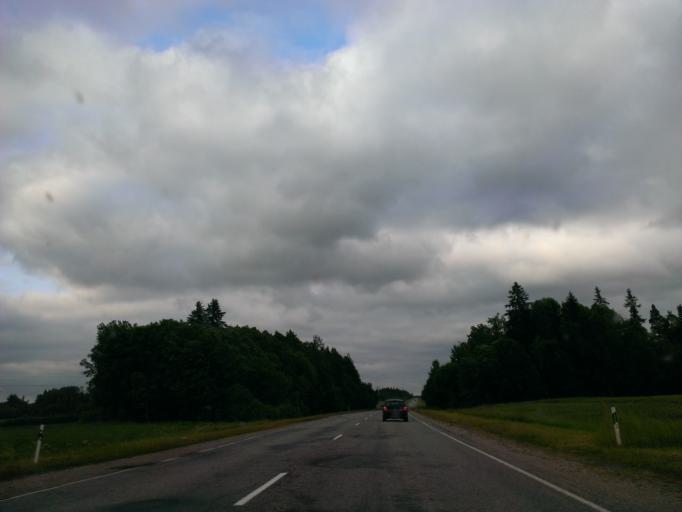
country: LV
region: Saldus Rajons
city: Saldus
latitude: 56.6720
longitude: 22.3813
